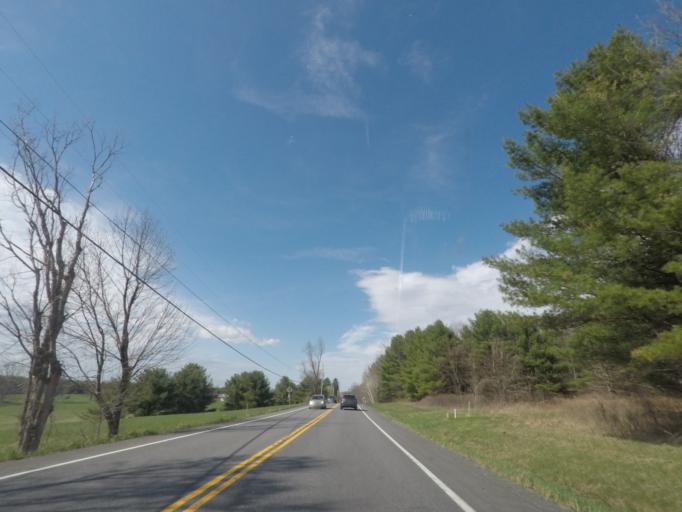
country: US
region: New York
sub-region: Greene County
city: Cairo
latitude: 42.4551
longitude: -74.0053
